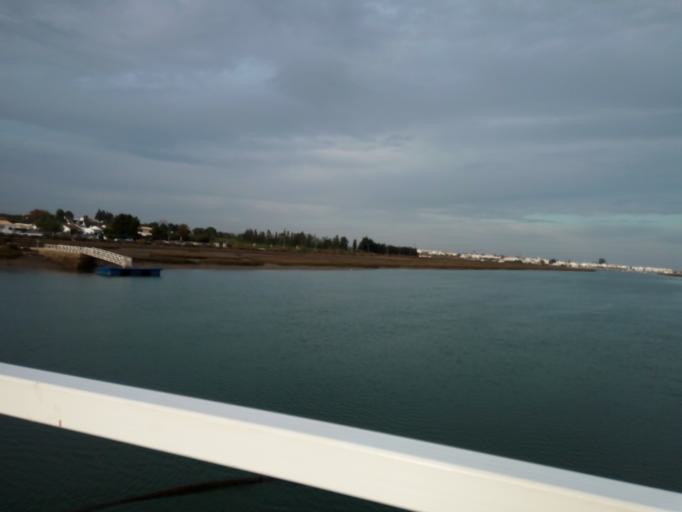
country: PT
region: Faro
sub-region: Tavira
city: Luz
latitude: 37.0916
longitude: -7.6734
